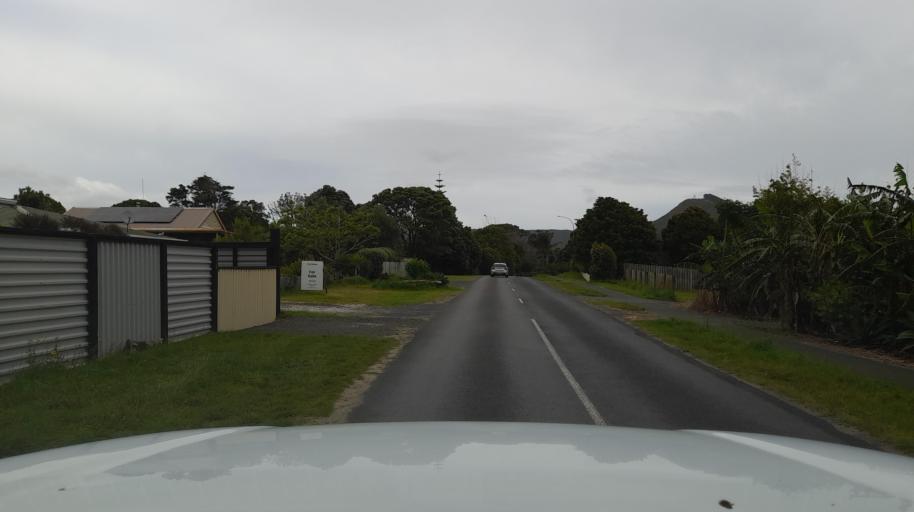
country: NZ
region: Northland
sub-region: Far North District
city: Ahipara
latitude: -35.1616
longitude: 173.1592
